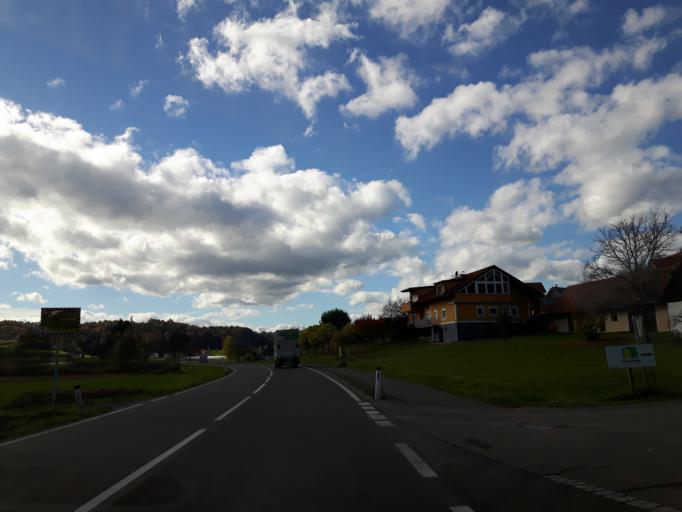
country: AT
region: Styria
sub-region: Politischer Bezirk Suedoststeiermark
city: Paldau
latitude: 46.9451
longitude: 15.8091
